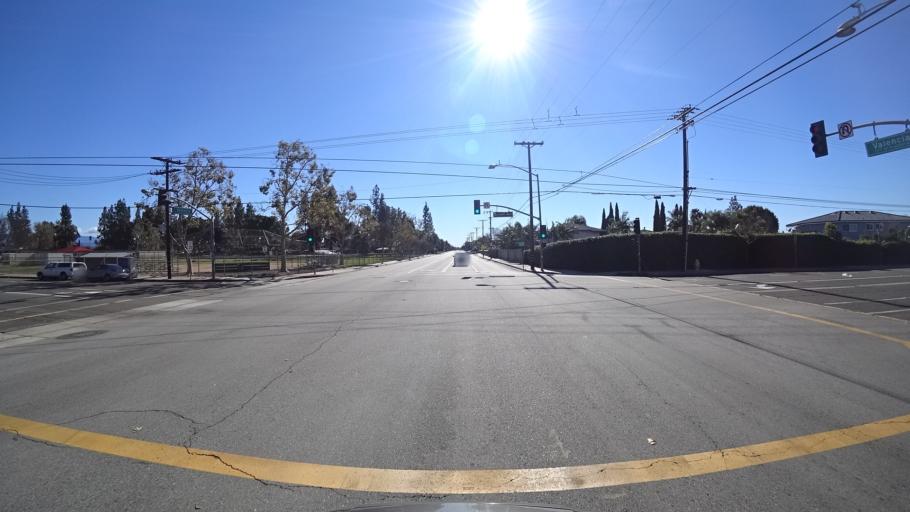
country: US
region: California
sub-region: Orange County
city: Placentia
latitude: 33.9041
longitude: -117.8551
